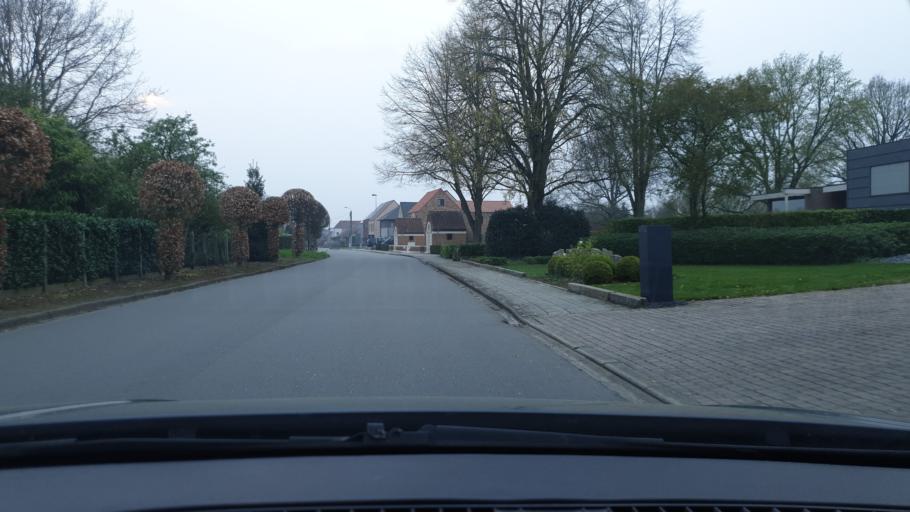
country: BE
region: Flanders
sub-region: Provincie Antwerpen
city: Geel
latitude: 51.1642
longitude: 5.0163
